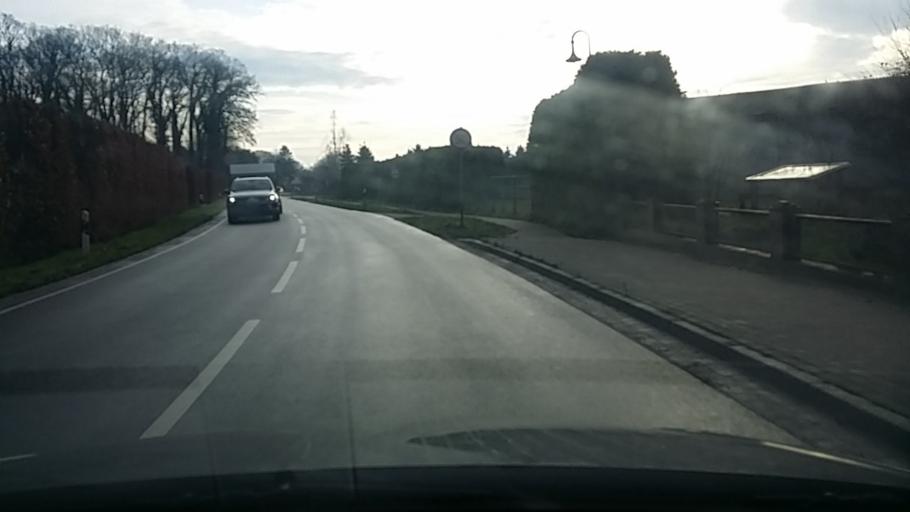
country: DE
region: Lower Saxony
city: Menslage
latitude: 52.6811
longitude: 7.8123
